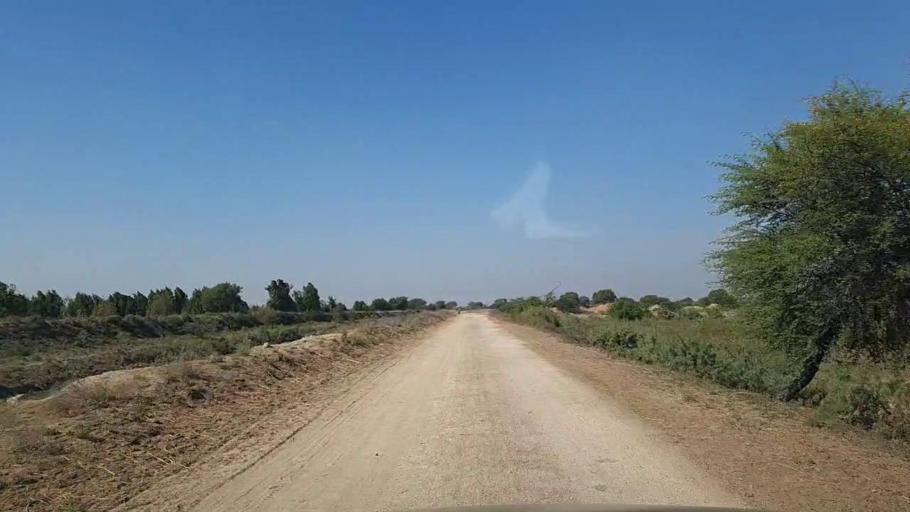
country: PK
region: Sindh
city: Mirpur Batoro
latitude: 24.7290
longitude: 68.2294
